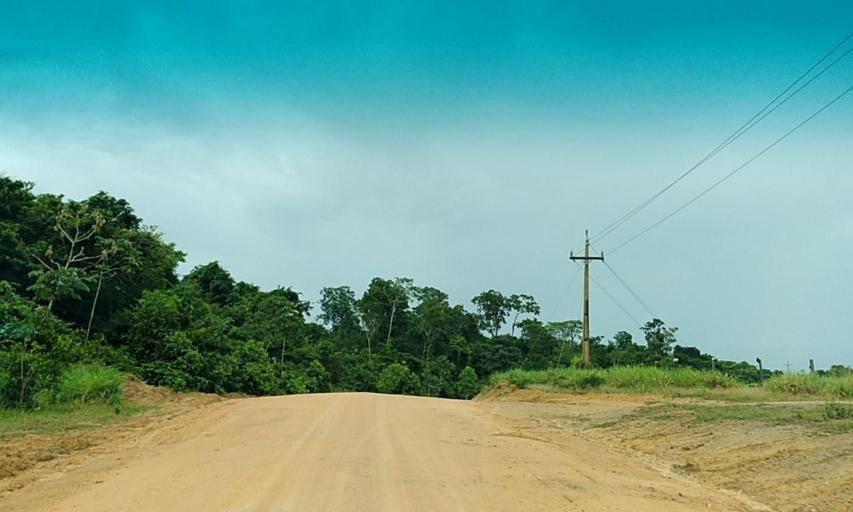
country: BR
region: Para
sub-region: Senador Jose Porfirio
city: Senador Jose Porfirio
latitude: -3.0584
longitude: -51.6731
